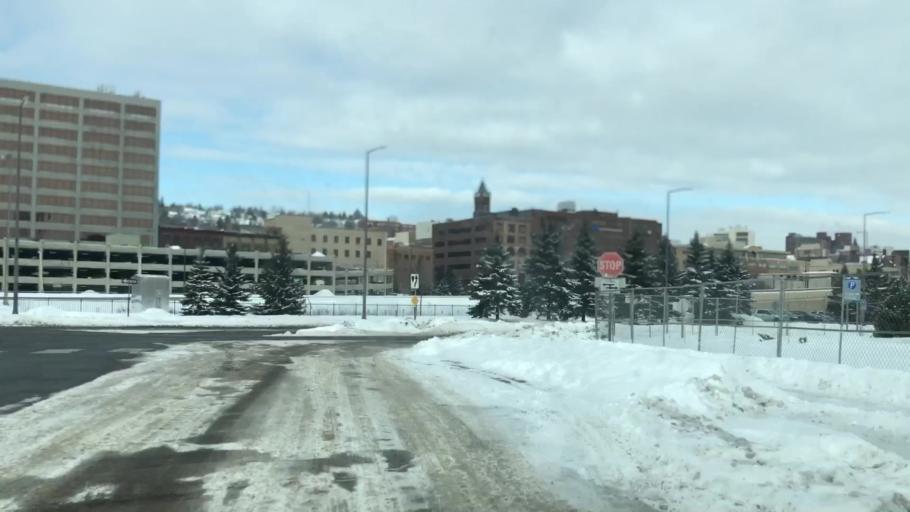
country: US
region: Minnesota
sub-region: Saint Louis County
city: Duluth
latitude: 46.7834
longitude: -92.0981
